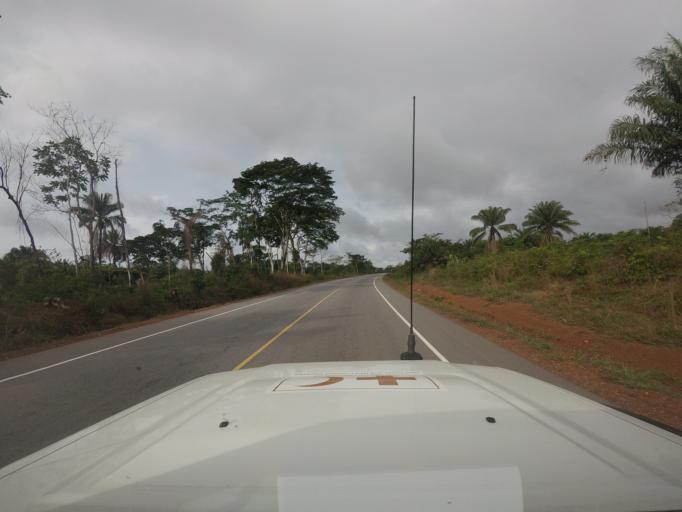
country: LR
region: Bong
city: Gbarnga
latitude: 7.0380
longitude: -9.2630
